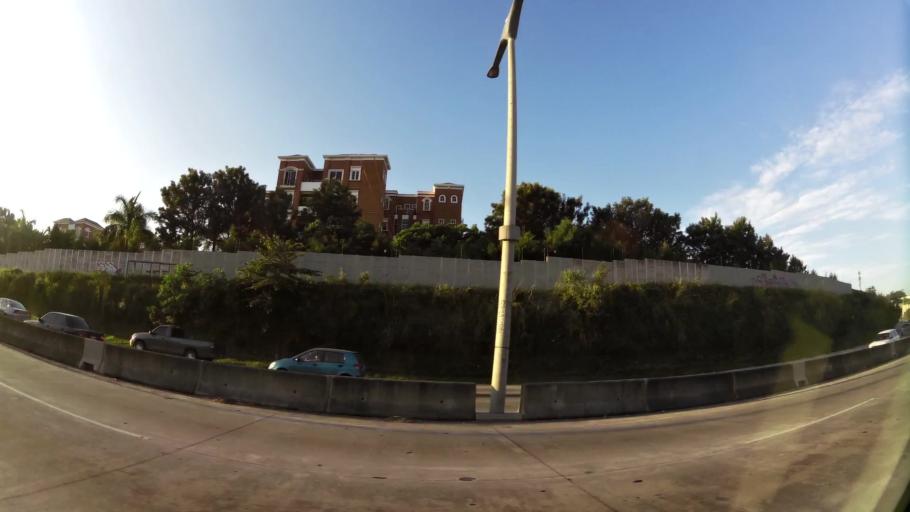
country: SV
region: La Libertad
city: Antiguo Cuscatlan
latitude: 13.6845
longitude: -89.2437
